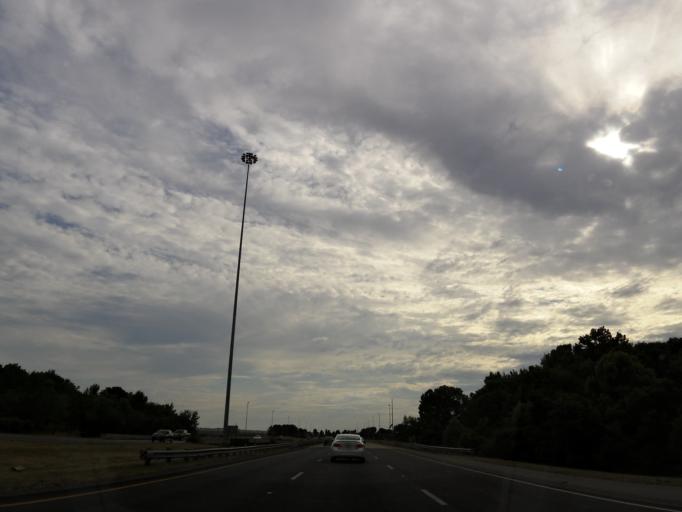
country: US
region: Alabama
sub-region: Madison County
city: Madison
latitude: 34.6711
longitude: -86.7586
